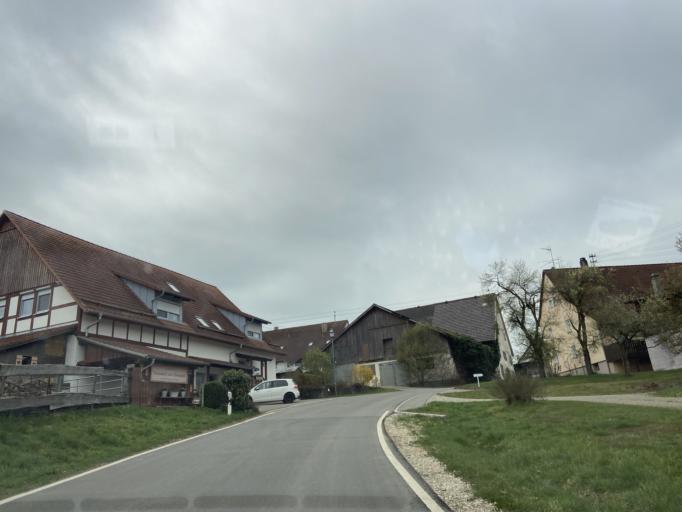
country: DE
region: Baden-Wuerttemberg
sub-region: Tuebingen Region
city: Inzigkofen
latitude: 48.0639
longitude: 9.1456
